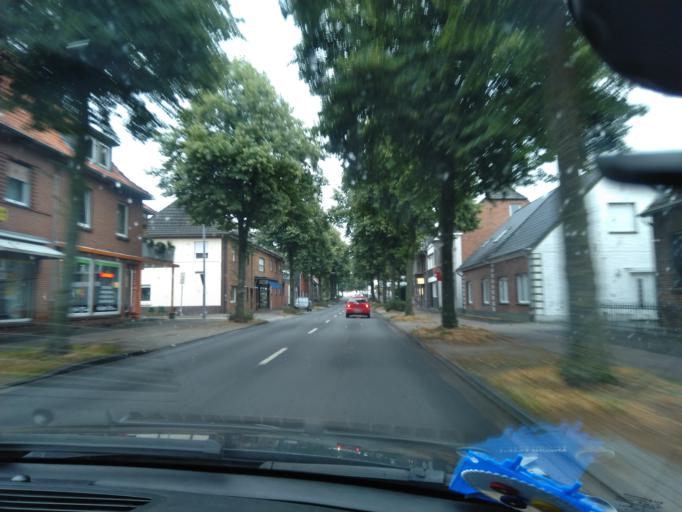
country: DE
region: Lower Saxony
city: Nordhorn
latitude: 52.4274
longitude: 7.0746
